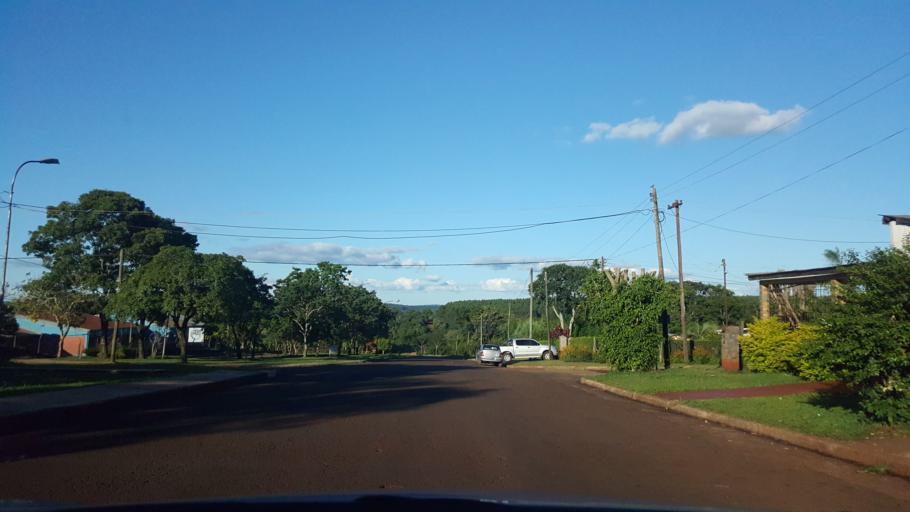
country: AR
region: Misiones
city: Gobernador Roca
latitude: -27.1267
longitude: -55.5075
